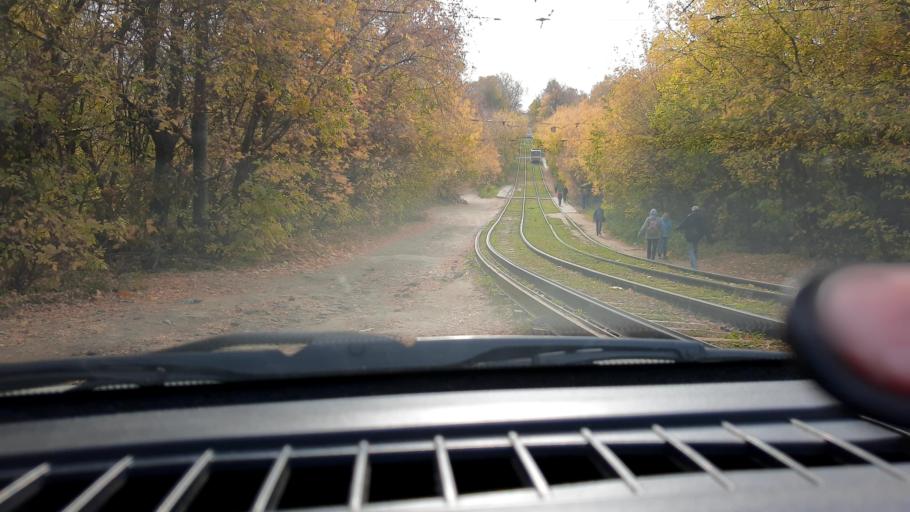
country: RU
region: Nizjnij Novgorod
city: Nizhniy Novgorod
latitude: 56.2951
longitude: 43.9941
